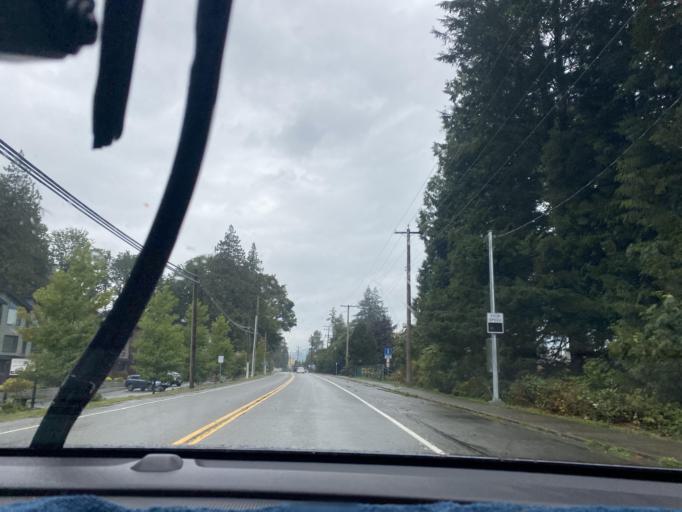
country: CA
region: British Columbia
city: Agassiz
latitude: 49.2970
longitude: -121.7843
